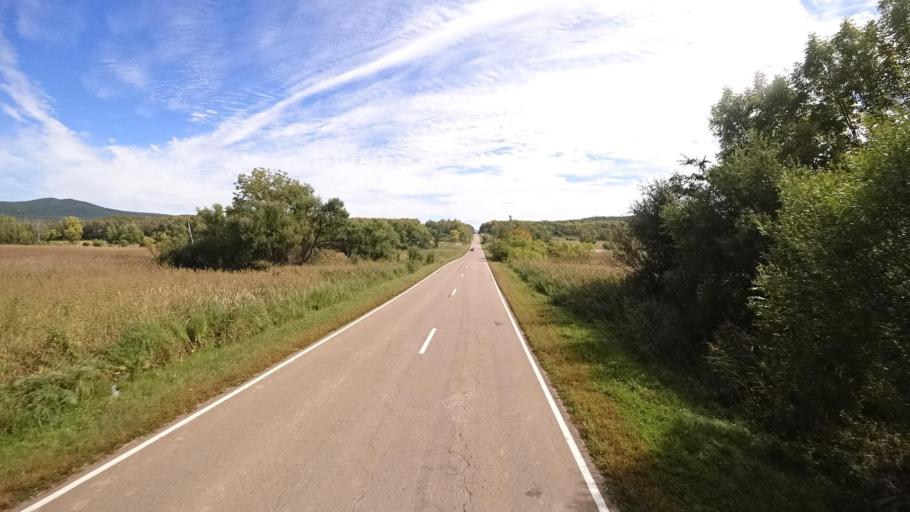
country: RU
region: Primorskiy
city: Yakovlevka
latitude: 44.4103
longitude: 133.5886
